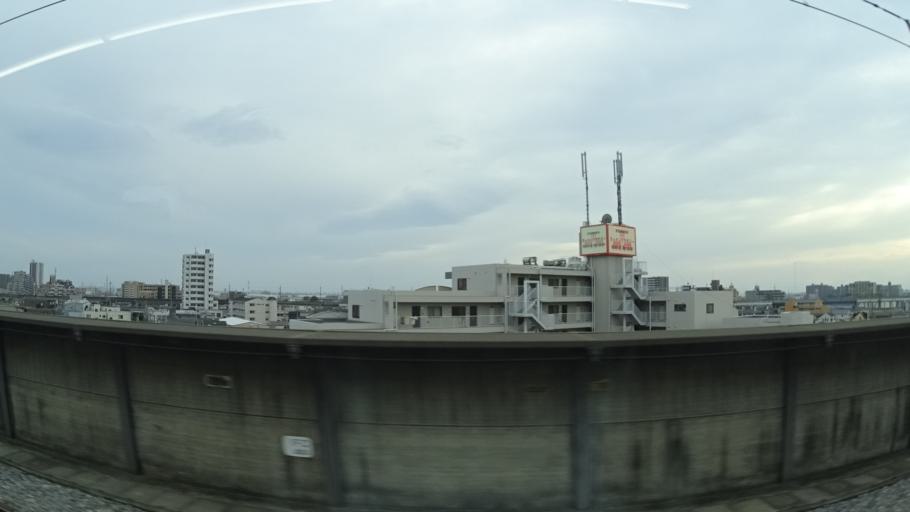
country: JP
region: Saitama
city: Yono
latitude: 35.8515
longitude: 139.6399
